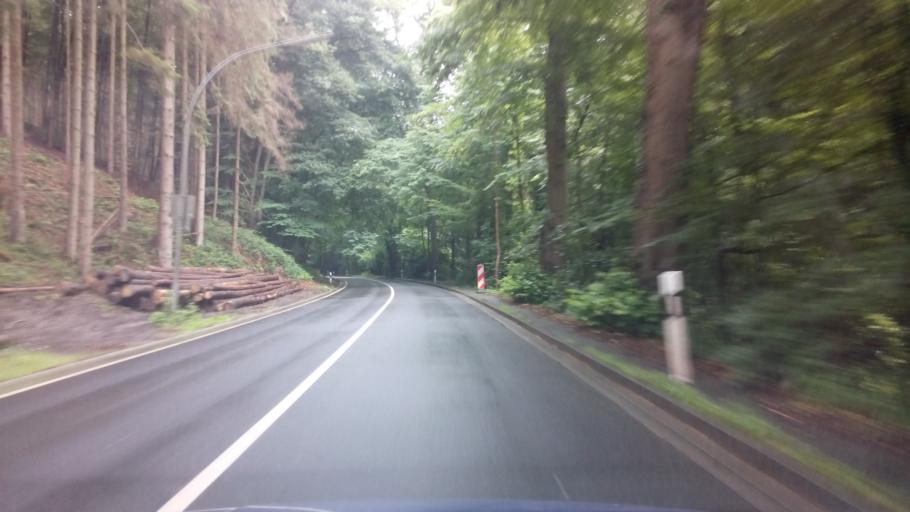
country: DE
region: Lower Saxony
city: Bad Essen
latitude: 52.3150
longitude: 8.3336
